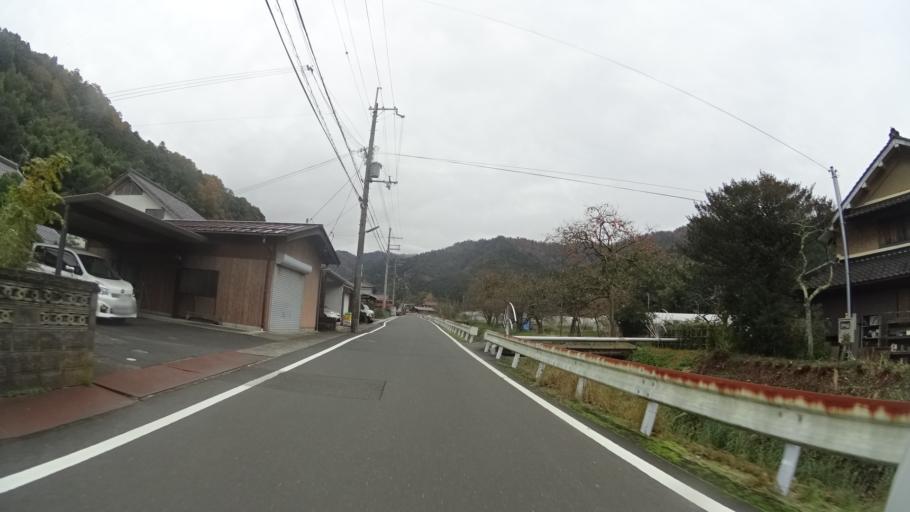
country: JP
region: Kyoto
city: Maizuru
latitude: 35.4797
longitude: 135.4416
